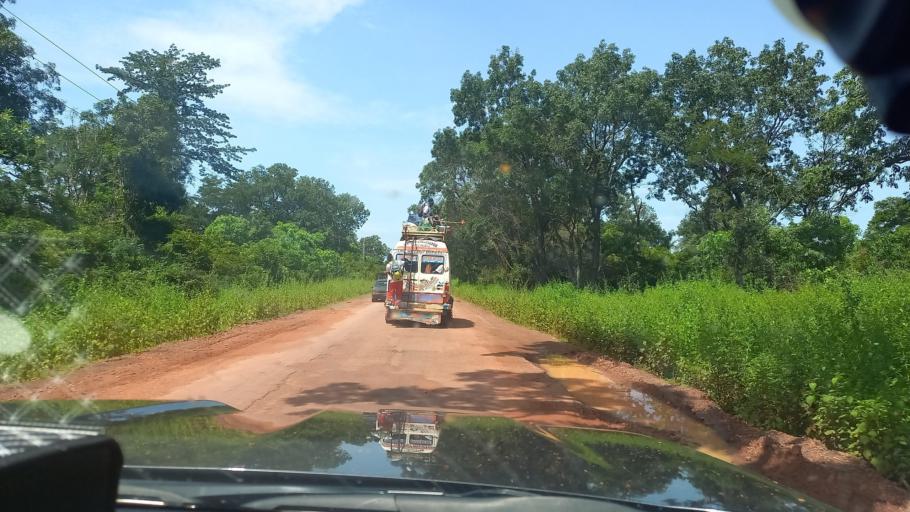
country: SN
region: Kolda
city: Marsassoum
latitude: 12.8574
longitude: -16.1054
